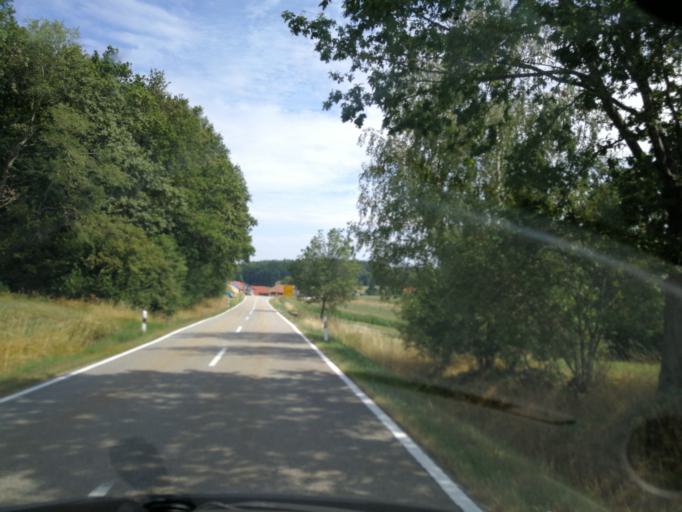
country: DE
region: Bavaria
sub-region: Lower Bavaria
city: Falkenfels
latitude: 49.0512
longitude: 12.5899
